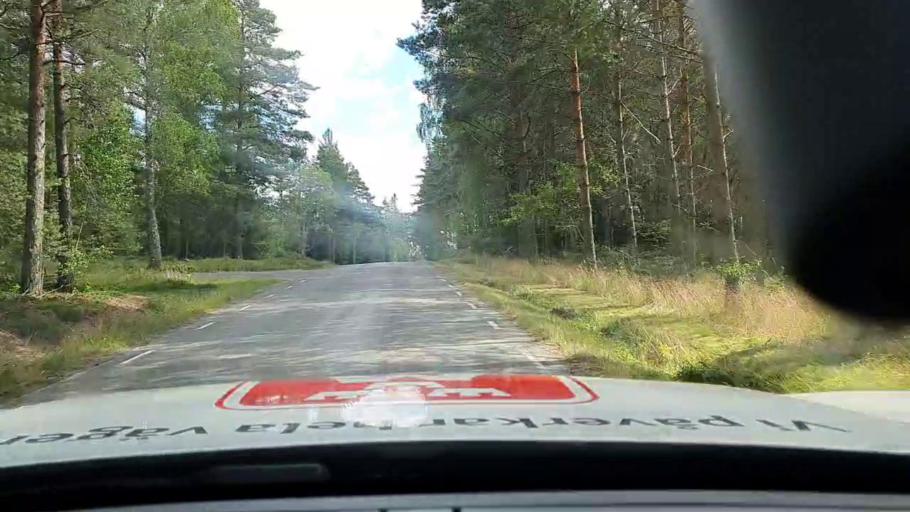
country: SE
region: Vaestra Goetaland
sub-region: Karlsborgs Kommun
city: Molltorp
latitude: 58.6118
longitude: 14.3596
